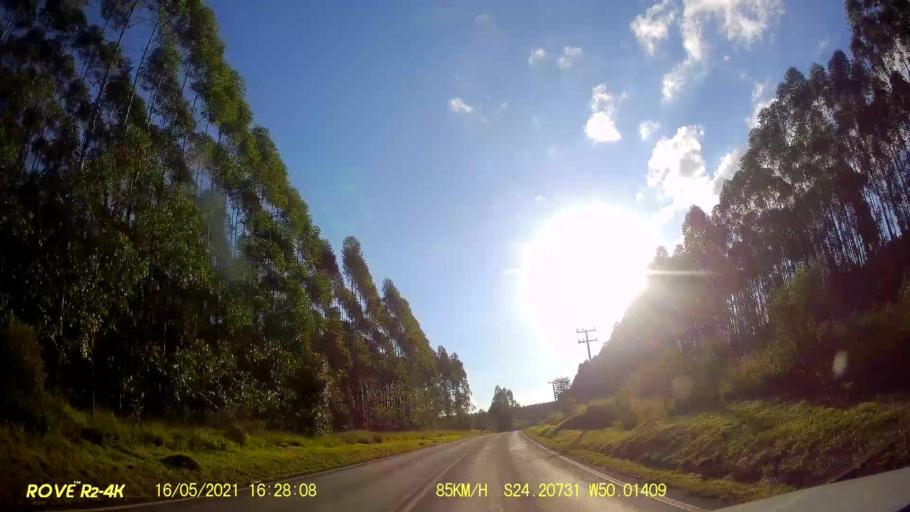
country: BR
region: Parana
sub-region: Jaguariaiva
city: Jaguariaiva
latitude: -24.2072
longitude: -50.0142
